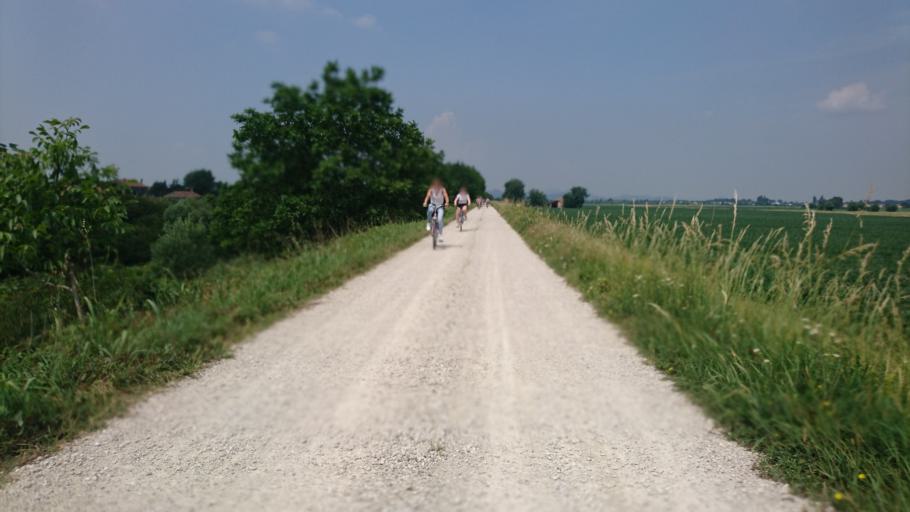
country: IT
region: Veneto
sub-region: Provincia di Padova
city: Bovolenta
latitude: 45.2762
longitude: 11.9106
